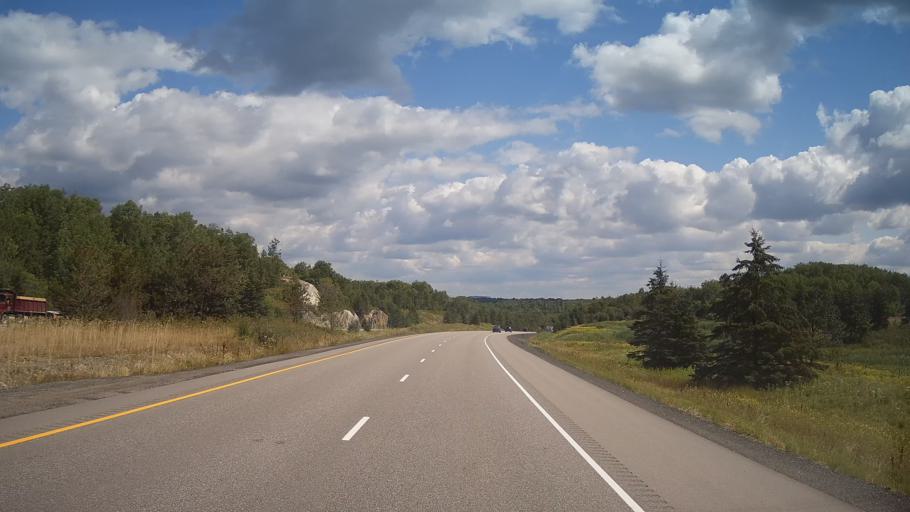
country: CA
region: Ontario
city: Rayside-Balfour
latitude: 46.3974
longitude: -81.3239
